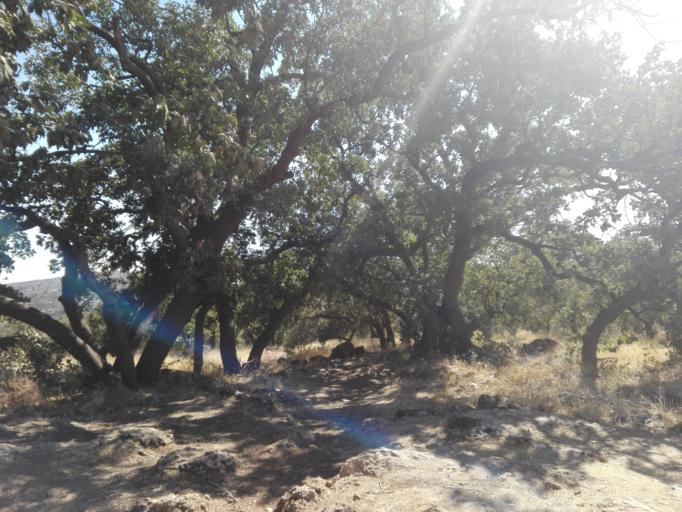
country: TR
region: Mardin
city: Kilavuz
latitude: 37.4787
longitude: 41.7768
